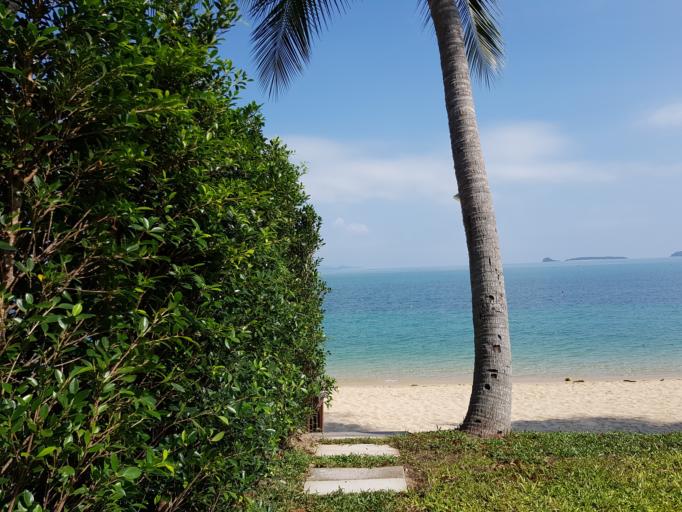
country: TH
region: Surat Thani
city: Ko Samui
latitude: 9.5635
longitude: 100.0225
